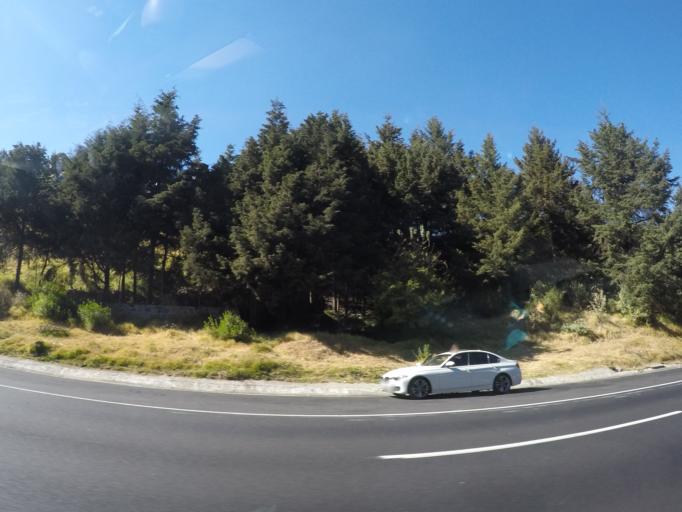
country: MX
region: Mexico City
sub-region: Cuajimalpa de Morelos
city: San Lorenzo Acopilco
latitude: 19.3191
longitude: -99.3215
